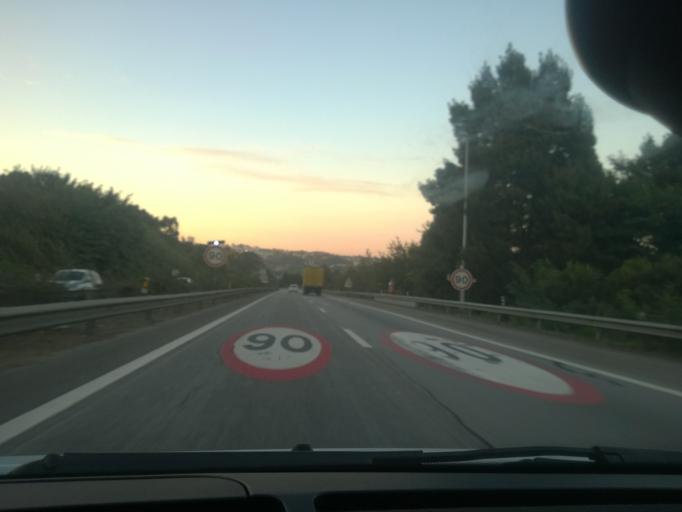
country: PT
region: Porto
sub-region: Vila Nova de Gaia
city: Oliveira do Douro
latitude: 41.1310
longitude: -8.5761
